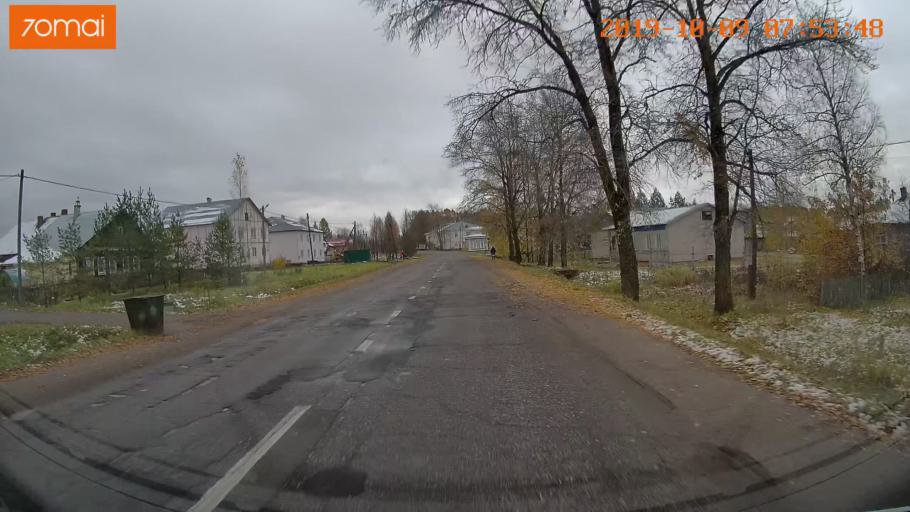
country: RU
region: Jaroslavl
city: Kukoboy
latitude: 58.6982
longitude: 39.8998
